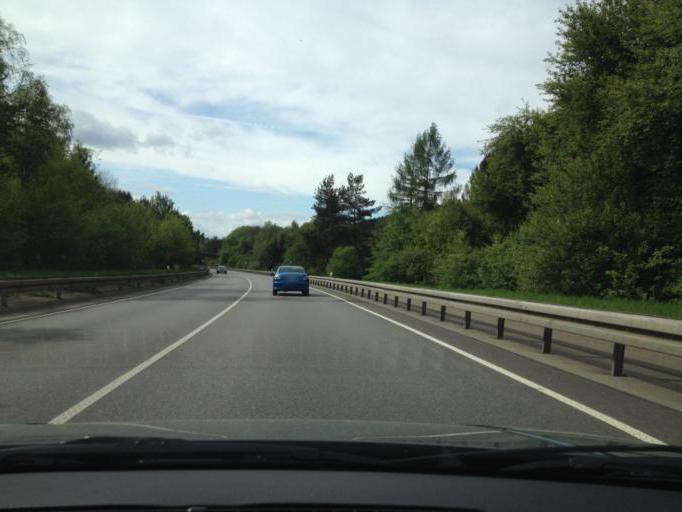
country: DE
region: Saarland
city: Bexbach
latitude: 49.3298
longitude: 7.2343
